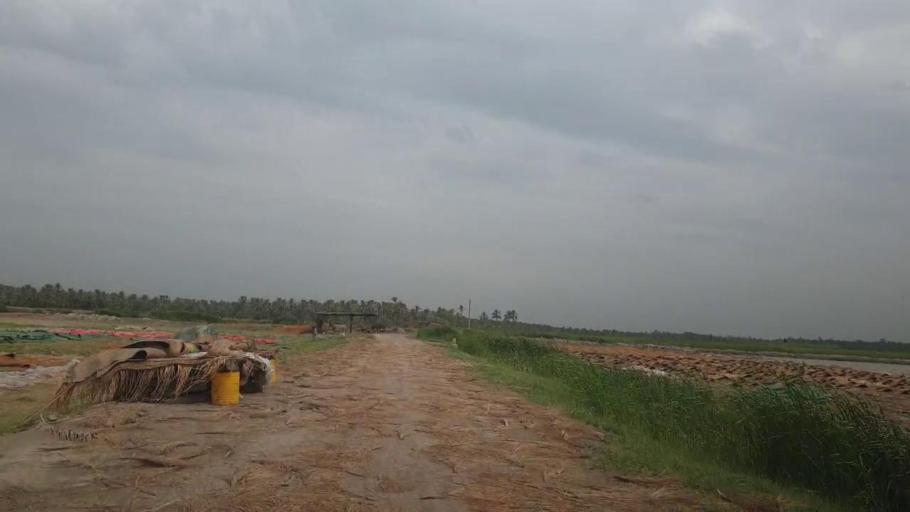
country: PK
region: Sindh
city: Khairpur
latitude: 27.5845
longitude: 68.7397
